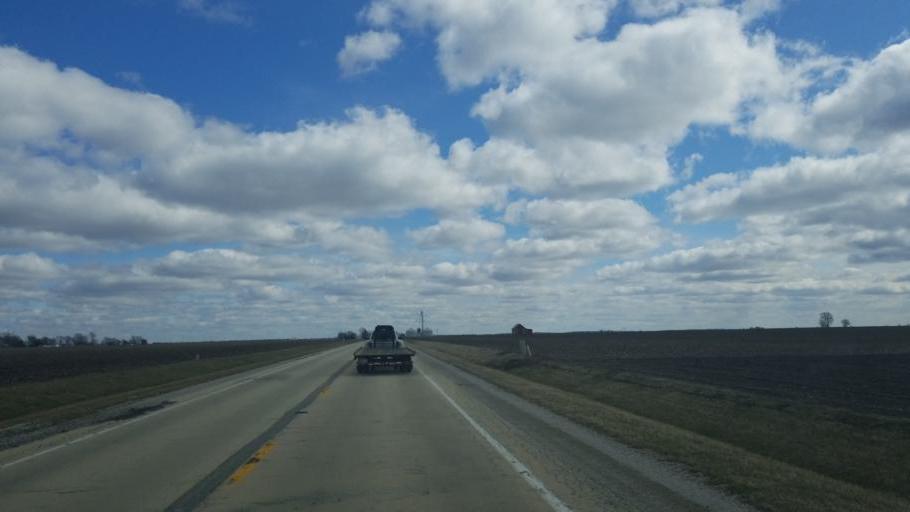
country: US
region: Illinois
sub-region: Douglas County
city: Atwood
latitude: 39.7920
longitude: -88.5408
